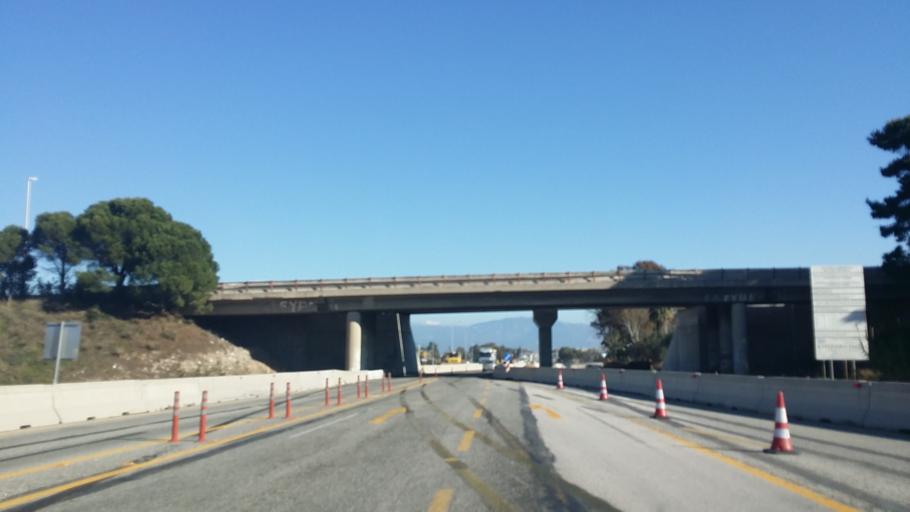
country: GR
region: West Greece
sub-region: Nomos Achaias
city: Rio
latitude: 38.2979
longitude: 21.7921
